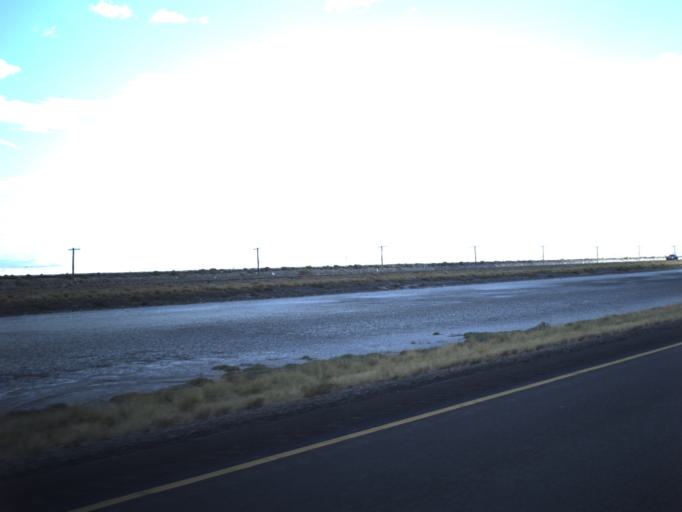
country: US
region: Utah
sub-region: Tooele County
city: Grantsville
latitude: 40.7223
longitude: -112.5632
